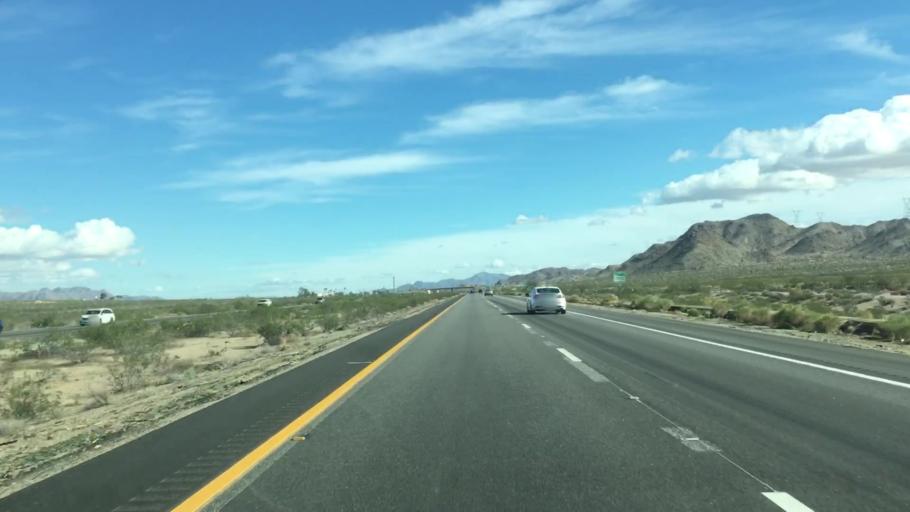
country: US
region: California
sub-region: Riverside County
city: Mecca
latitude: 33.6599
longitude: -115.7375
